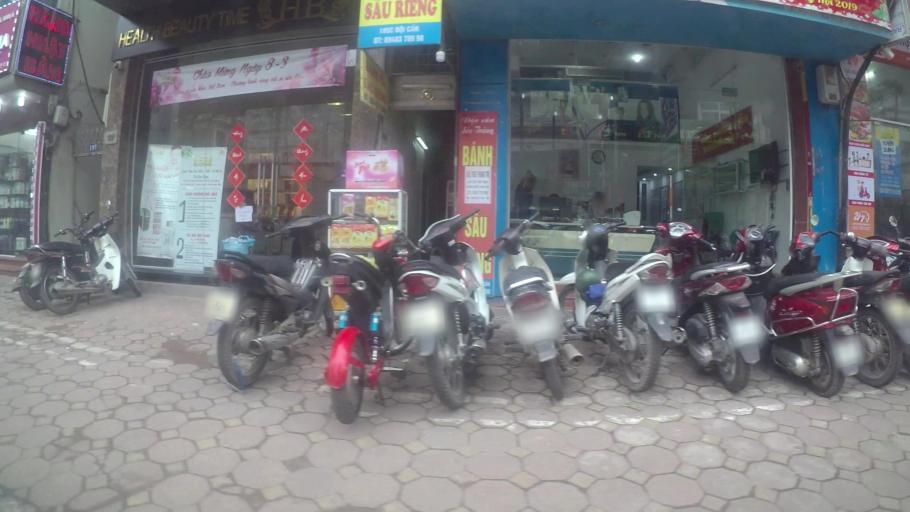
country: VN
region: Ha Noi
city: Dong Da
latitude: 21.0351
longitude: 105.8232
